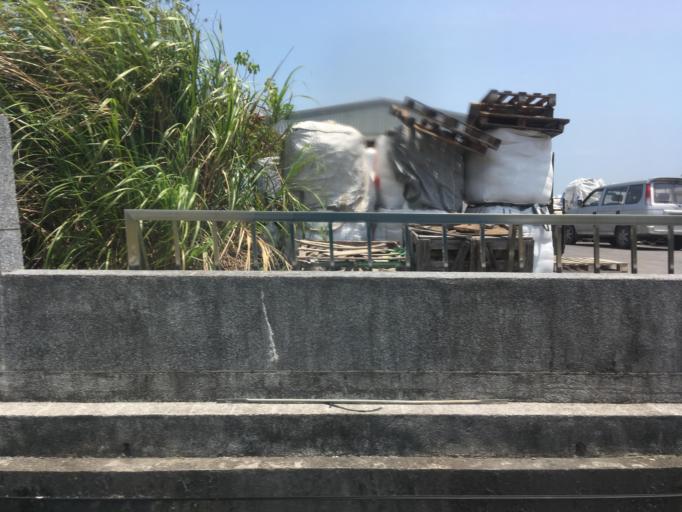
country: TW
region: Taiwan
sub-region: Yilan
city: Yilan
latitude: 24.6746
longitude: 121.8036
